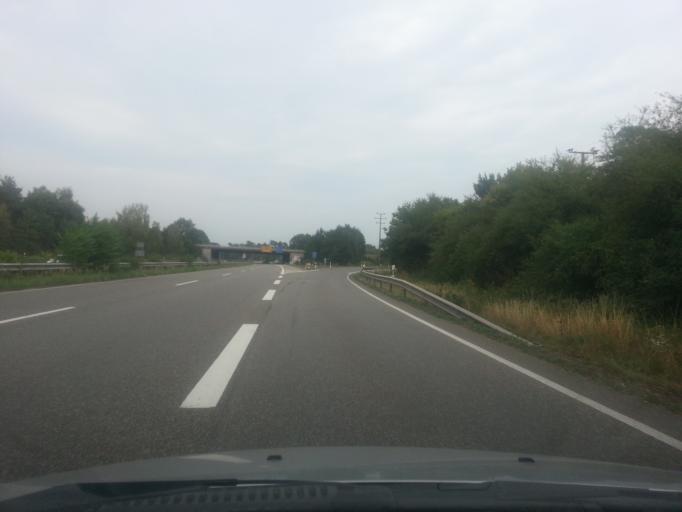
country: DE
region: Rheinland-Pfalz
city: Speyer
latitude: 49.3512
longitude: 8.4205
